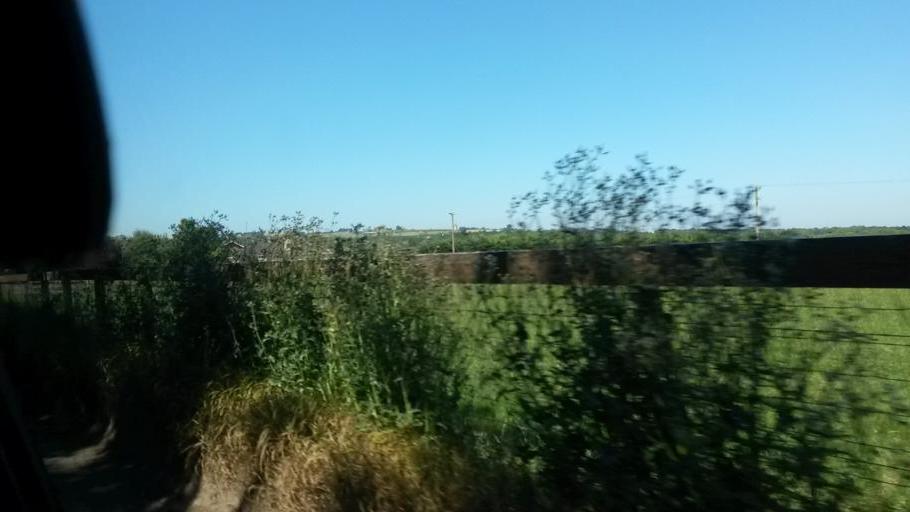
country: IE
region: Leinster
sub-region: An Mhi
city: Stamullin
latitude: 53.5386
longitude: -6.2711
